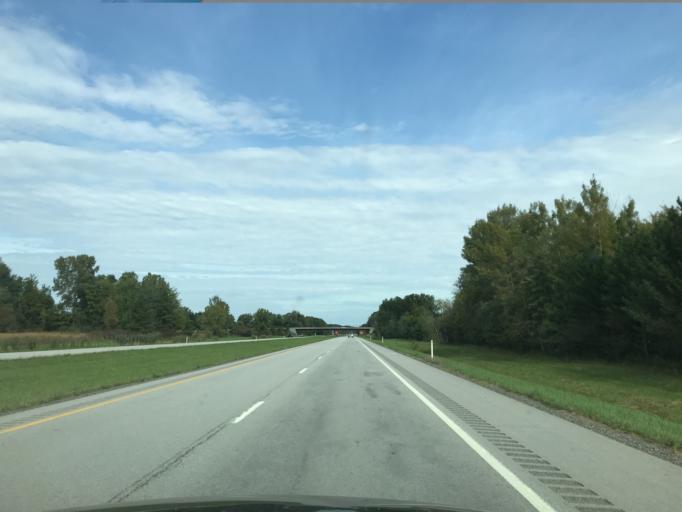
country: US
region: Ohio
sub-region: Ashtabula County
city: Jefferson
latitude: 41.6764
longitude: -80.7134
